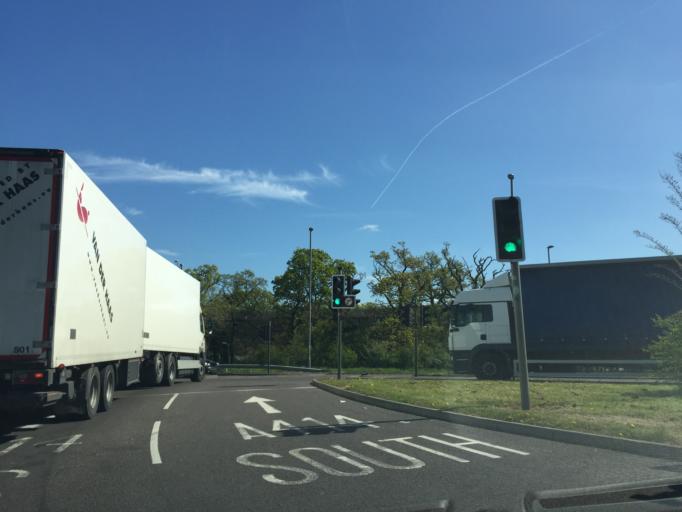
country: GB
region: England
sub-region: Essex
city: Harlow
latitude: 51.7564
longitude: 0.1271
